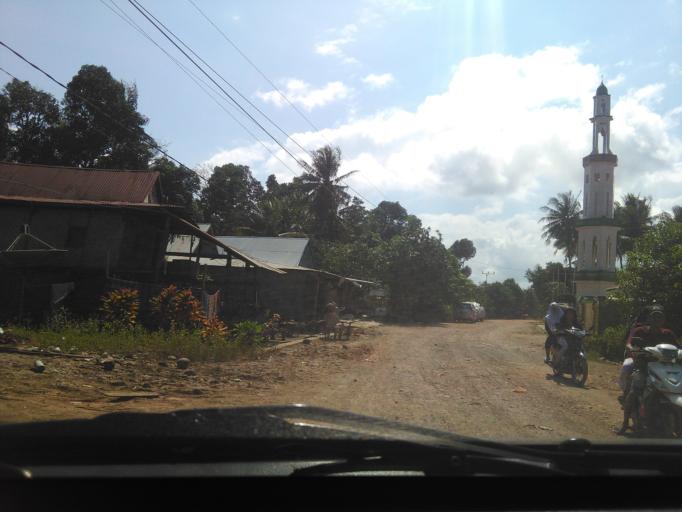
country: ID
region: South Sulawesi
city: Tancung
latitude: -4.0150
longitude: 119.9251
